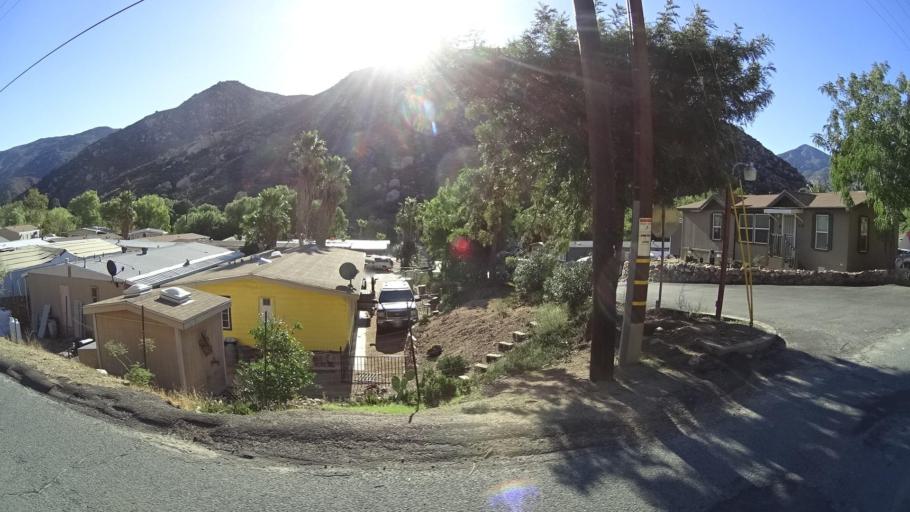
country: MX
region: Baja California
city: Tecate
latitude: 32.6230
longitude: -116.6917
